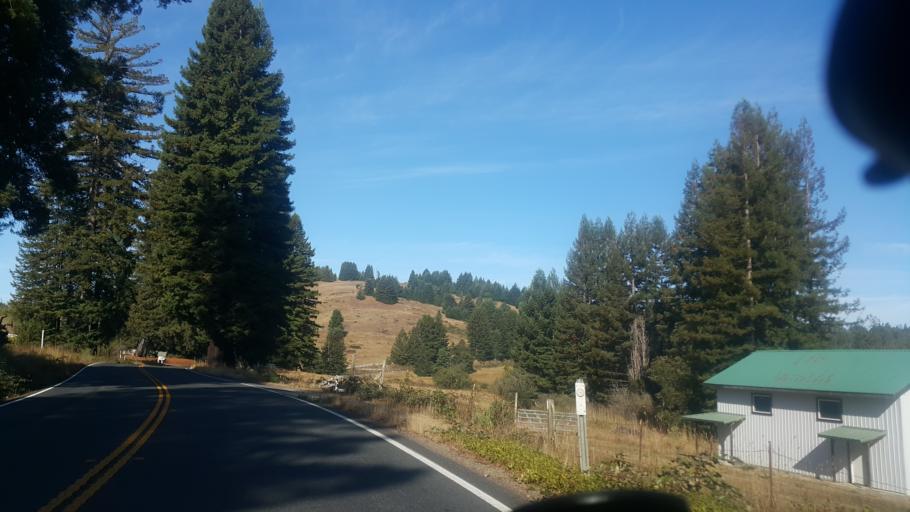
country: US
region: California
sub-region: Mendocino County
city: Fort Bragg
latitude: 39.3536
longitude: -123.6101
